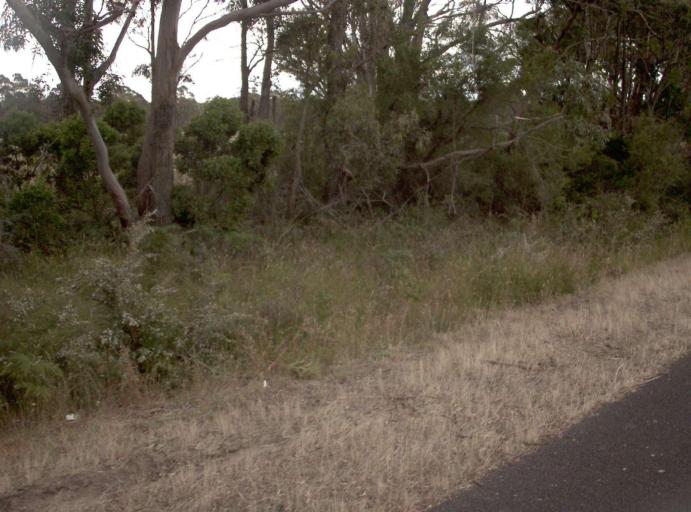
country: AU
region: Victoria
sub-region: Wellington
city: Sale
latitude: -38.4715
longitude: 146.9287
